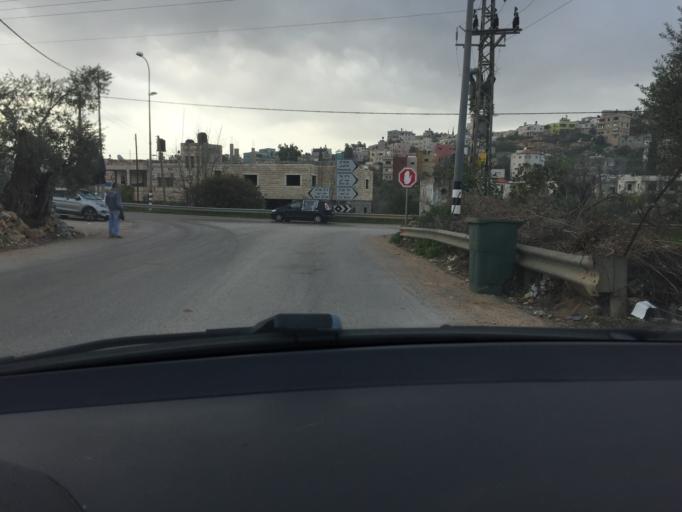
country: PS
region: West Bank
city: Al Lubban al Gharbi
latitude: 32.0383
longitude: 35.0407
